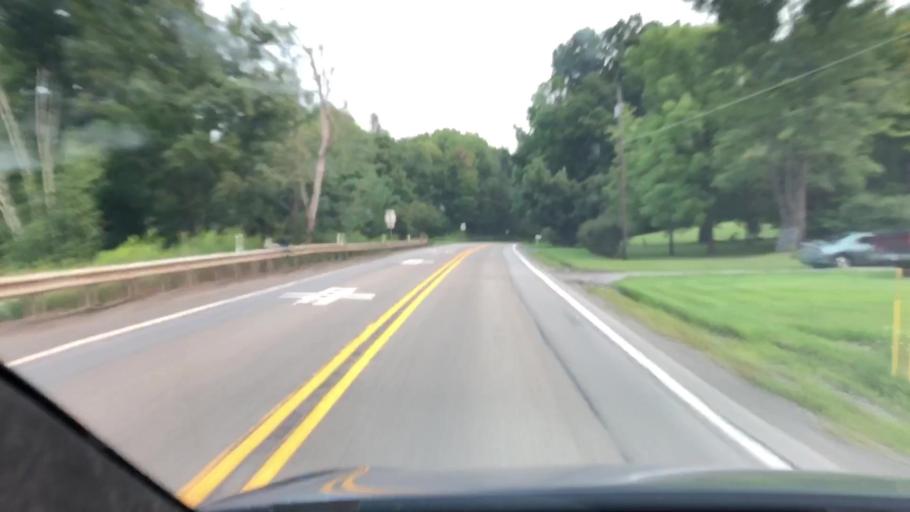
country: US
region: Pennsylvania
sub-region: Butler County
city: Slippery Rock
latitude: 41.0924
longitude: -80.0021
